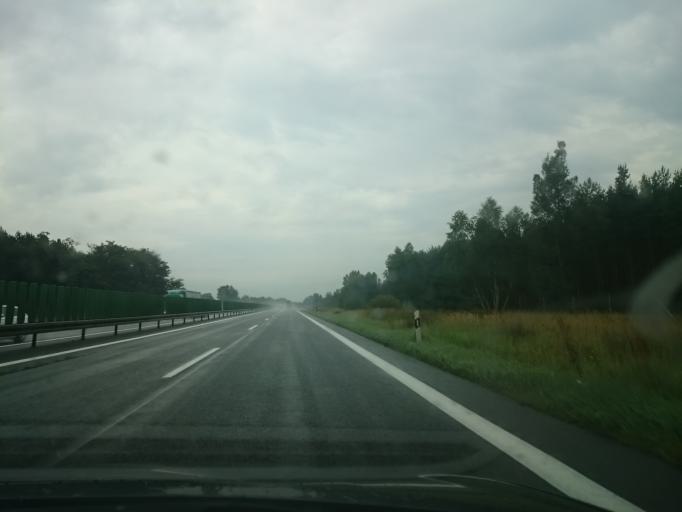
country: DE
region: Brandenburg
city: Brieselang
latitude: 52.6702
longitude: 13.0059
